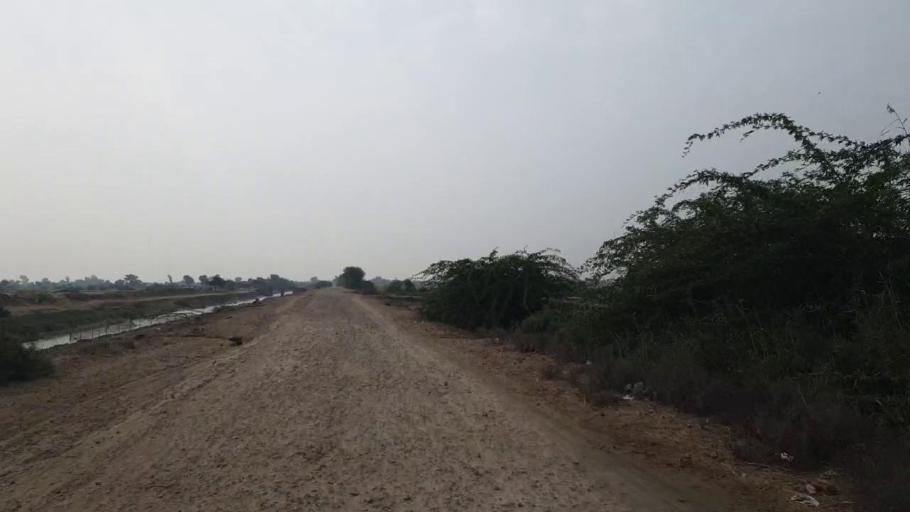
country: PK
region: Sindh
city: Kario
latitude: 24.8897
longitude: 68.5261
